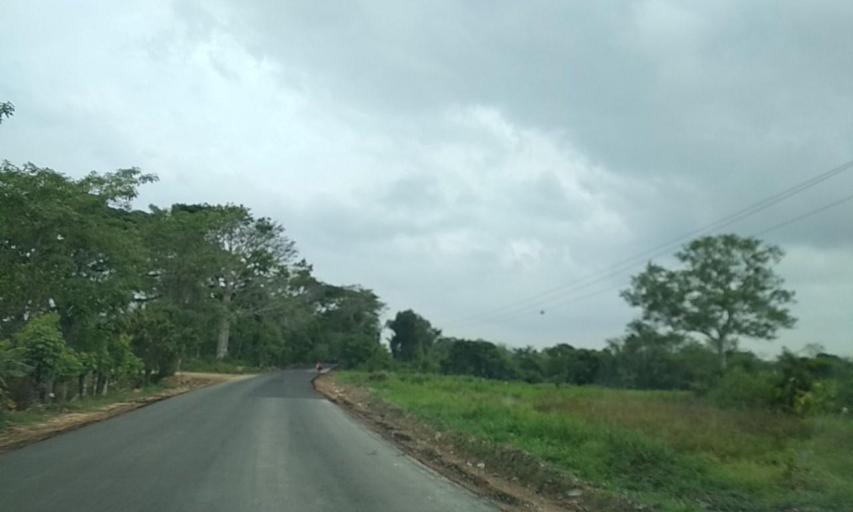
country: MX
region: Tabasco
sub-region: Huimanguillo
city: Francisco Rueda
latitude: 17.6795
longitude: -94.0922
